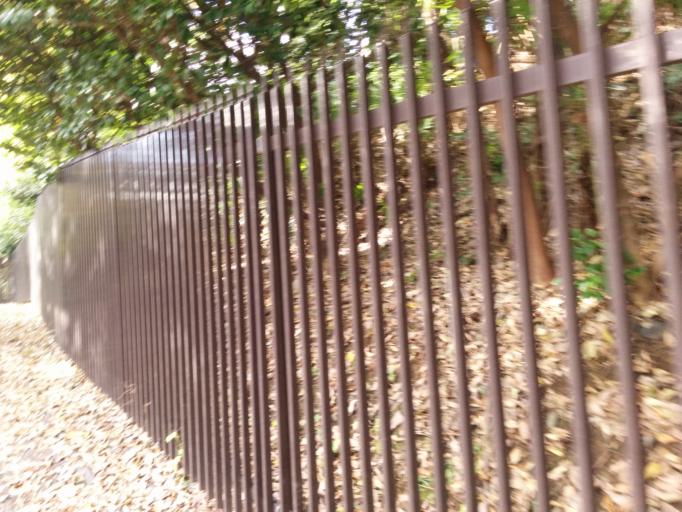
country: JP
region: Tokyo
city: Tokyo
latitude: 35.7060
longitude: 139.7144
